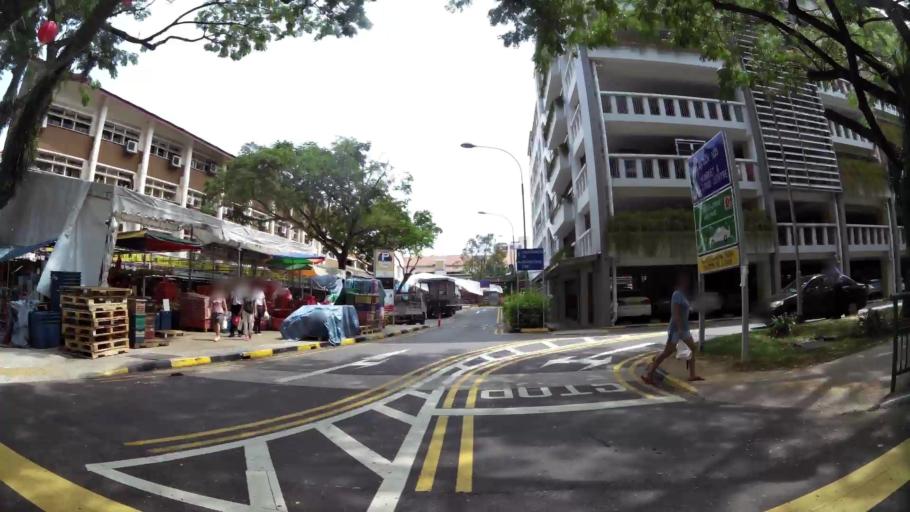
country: MY
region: Johor
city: Johor Bahru
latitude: 1.3496
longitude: 103.7176
